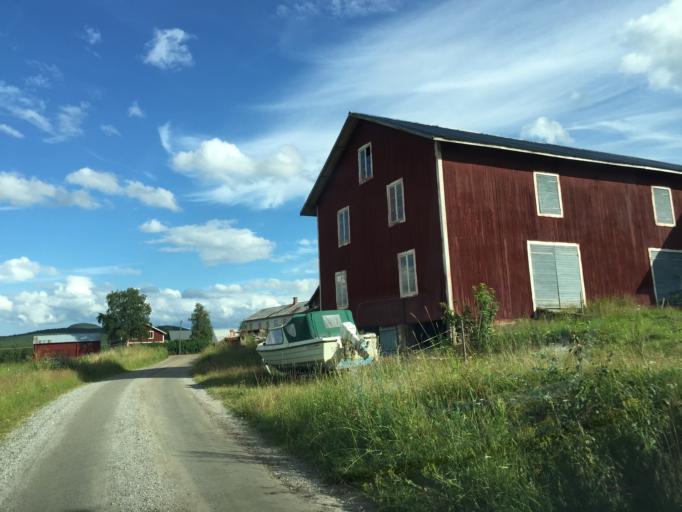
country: SE
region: Gaevleborg
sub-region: Ljusdals Kommun
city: Jaervsoe
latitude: 61.7547
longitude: 16.1687
